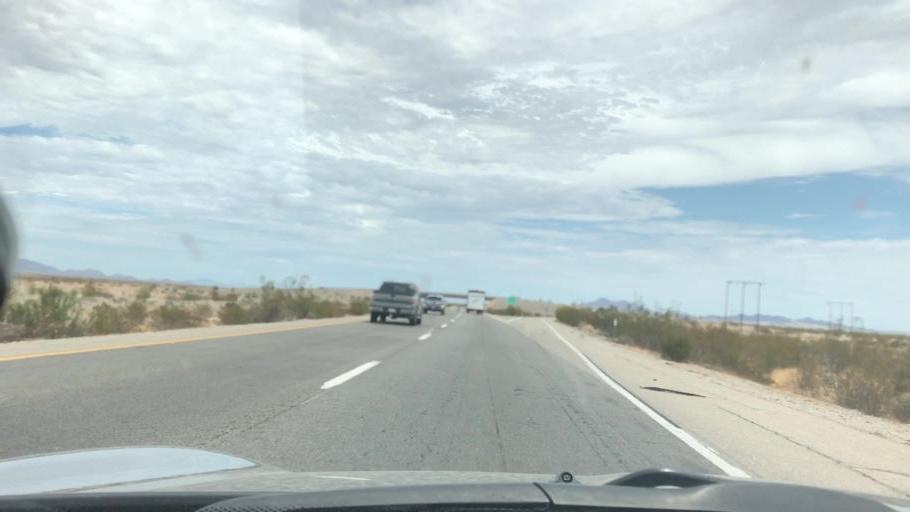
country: US
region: California
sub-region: Riverside County
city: Mesa Verde
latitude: 33.6084
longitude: -114.9942
